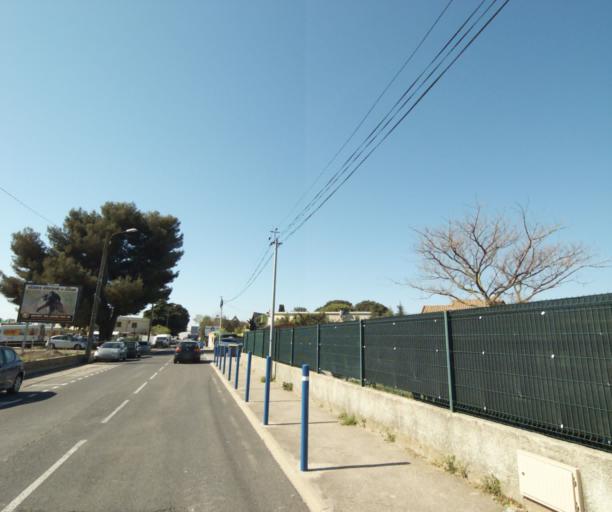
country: FR
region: Languedoc-Roussillon
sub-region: Departement de l'Herault
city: Le Cres
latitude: 43.6407
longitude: 3.9346
